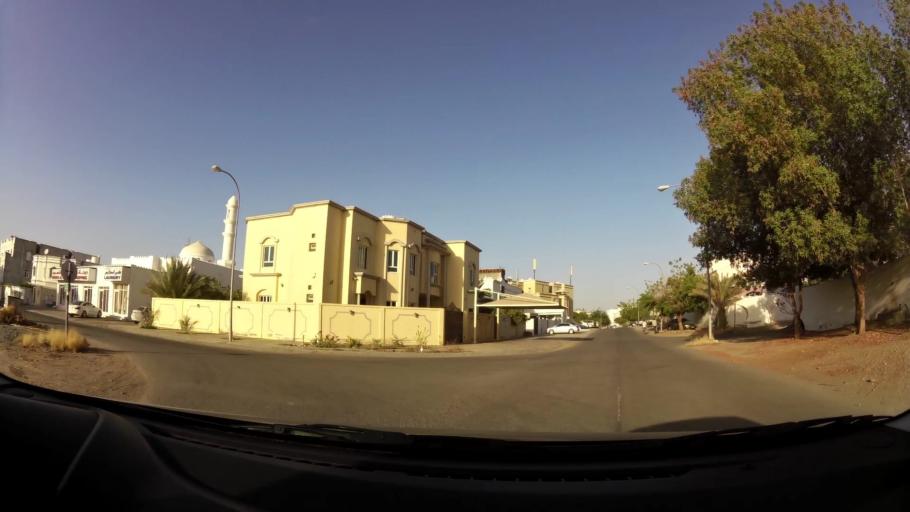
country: OM
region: Muhafazat Masqat
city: As Sib al Jadidah
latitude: 23.6099
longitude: 58.2323
